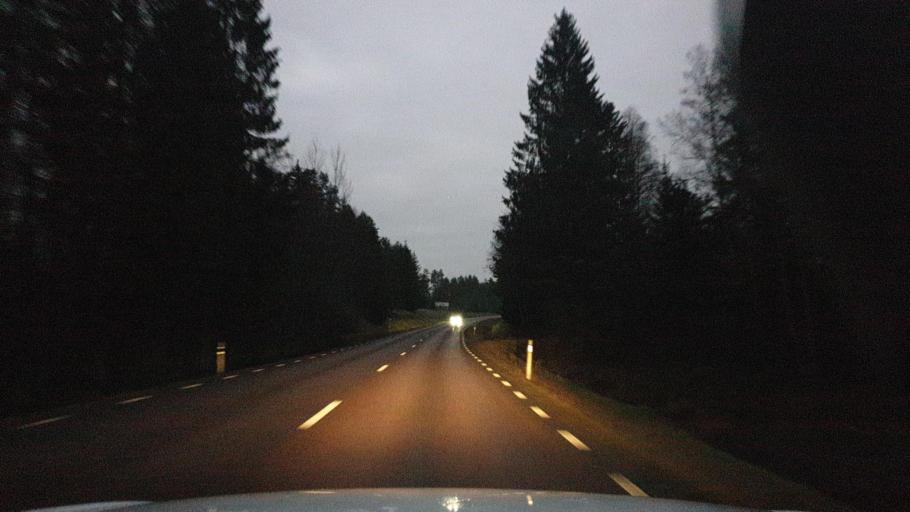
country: SE
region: Vaermland
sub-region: Eda Kommun
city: Charlottenberg
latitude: 59.9162
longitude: 12.2713
